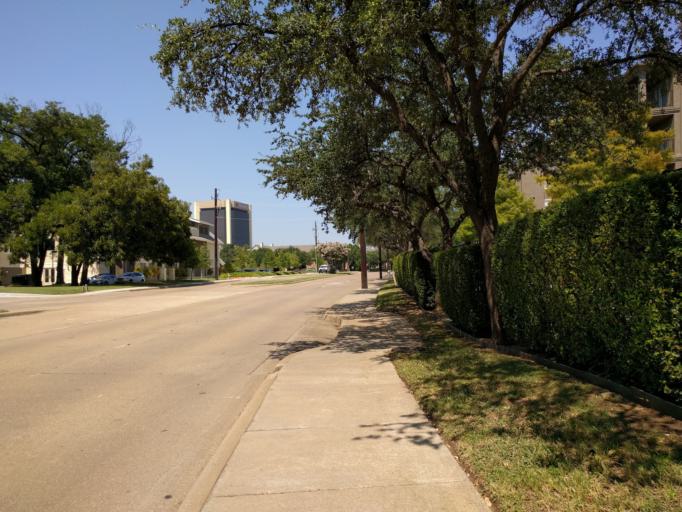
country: US
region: Texas
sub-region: Dallas County
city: Richardson
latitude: 32.9167
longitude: -96.7726
